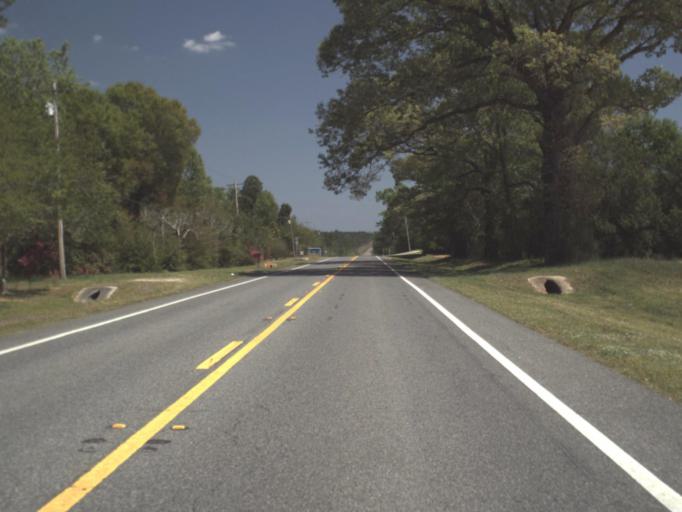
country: US
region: Alabama
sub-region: Escambia County
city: East Brewton
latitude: 30.9521
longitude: -87.1122
